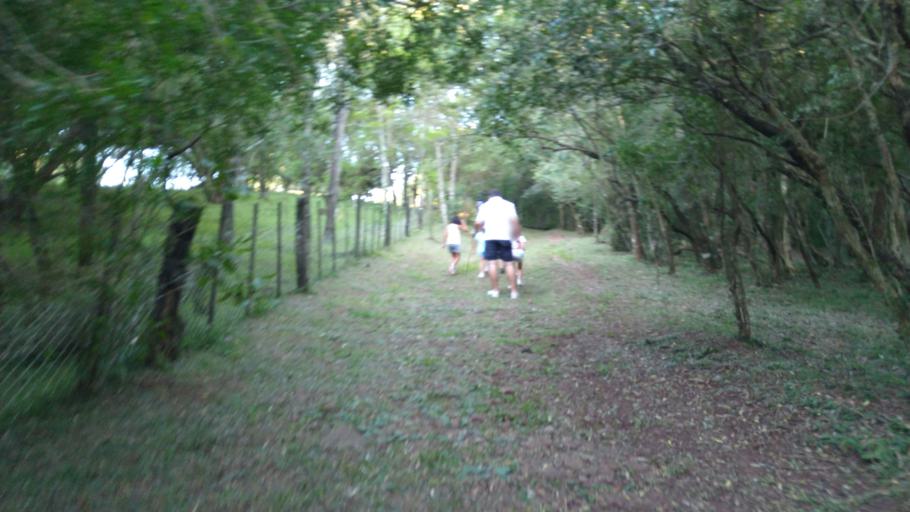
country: AR
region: Misiones
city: Garupa
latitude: -27.4925
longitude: -55.8208
